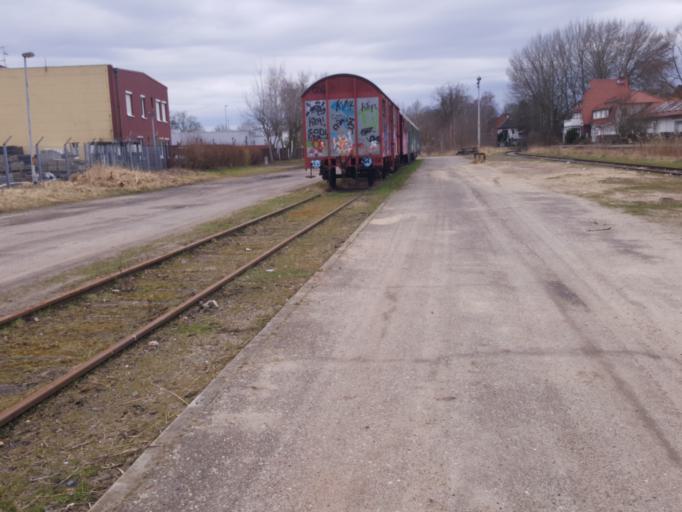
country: DE
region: Hamburg
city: Bergedorf
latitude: 53.4822
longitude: 10.2138
